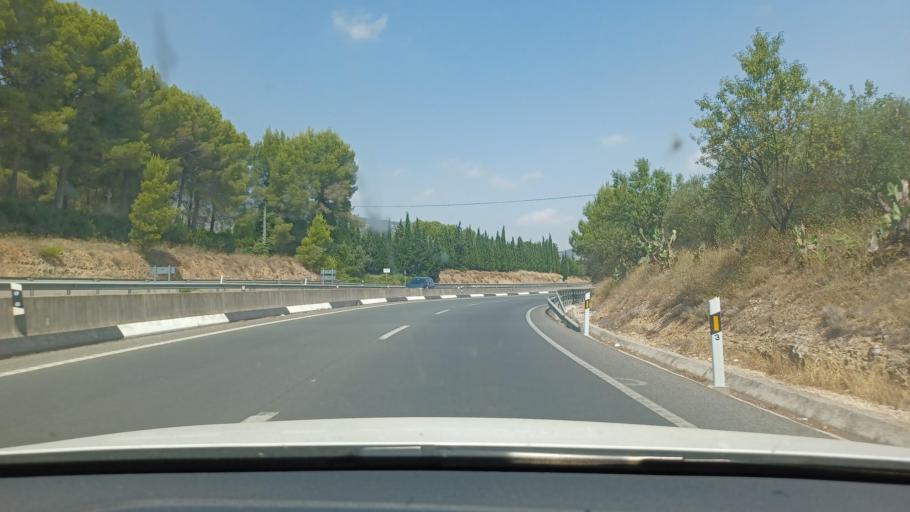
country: ES
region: Valencia
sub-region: Provincia de Alicante
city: Cocentaina
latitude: 38.7600
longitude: -0.4426
